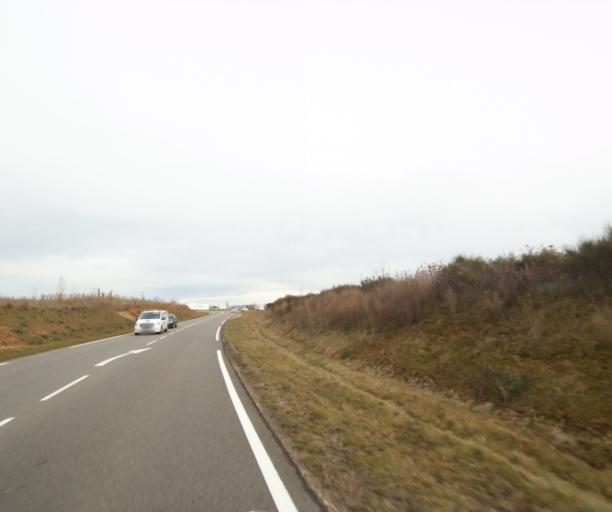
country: FR
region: Rhone-Alpes
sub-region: Departement de la Loire
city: Sury-le-Comtal
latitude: 45.5194
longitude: 4.1909
